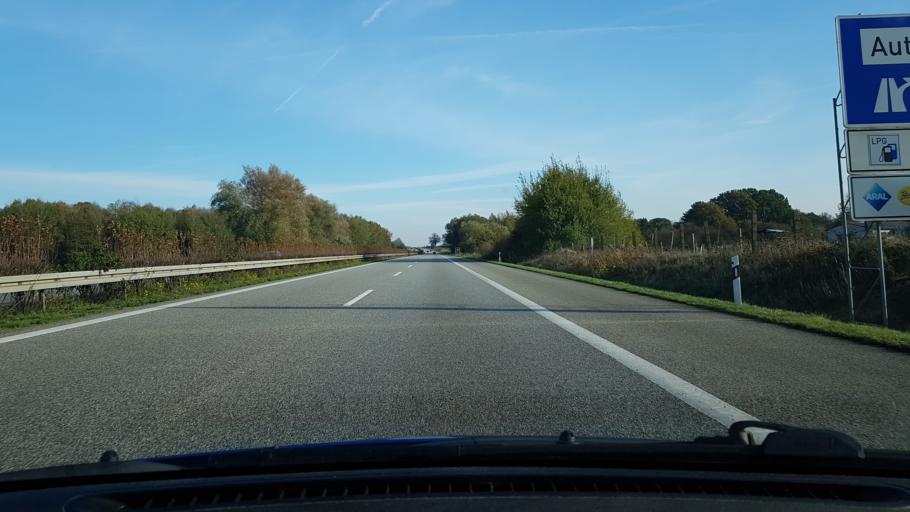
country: DE
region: Mecklenburg-Vorpommern
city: Wittenburg
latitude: 53.5005
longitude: 11.0568
